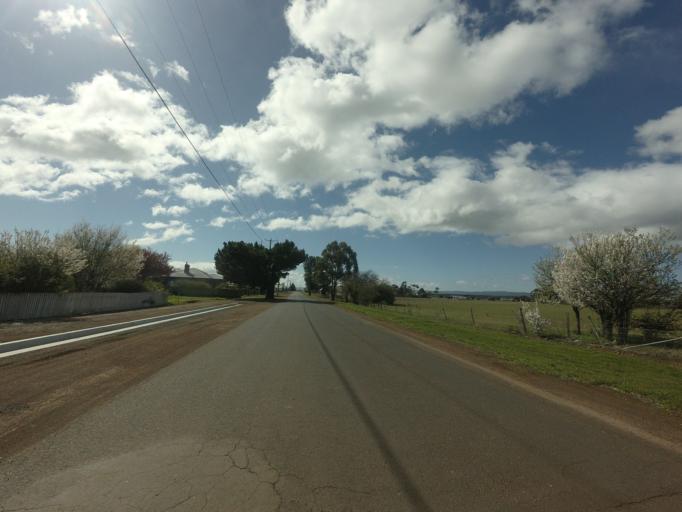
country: AU
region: Tasmania
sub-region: Northern Midlands
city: Evandale
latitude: -42.1392
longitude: 147.4249
